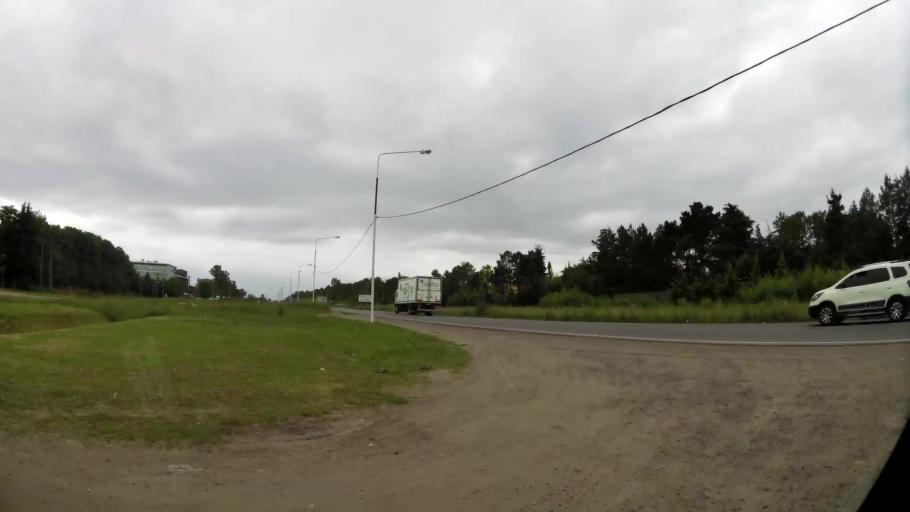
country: AR
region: Buenos Aires
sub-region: Partido de Ezeiza
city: Ezeiza
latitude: -34.8880
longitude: -58.5059
